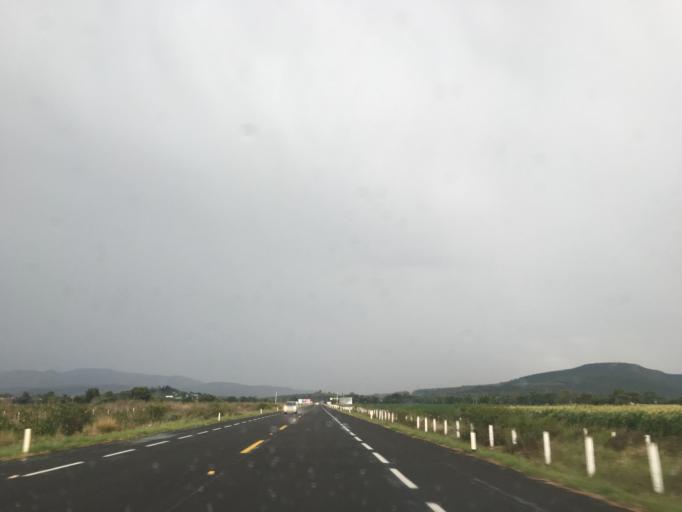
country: MX
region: Michoacan
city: Alvaro Obregon
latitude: 19.8338
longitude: -101.0107
